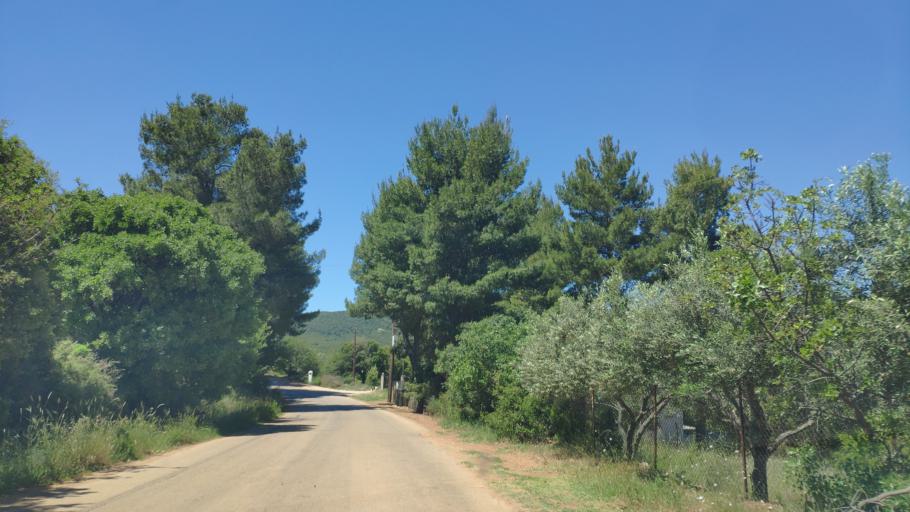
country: GR
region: Central Greece
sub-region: Nomos Voiotias
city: Kaparellion
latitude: 38.2142
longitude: 23.1951
